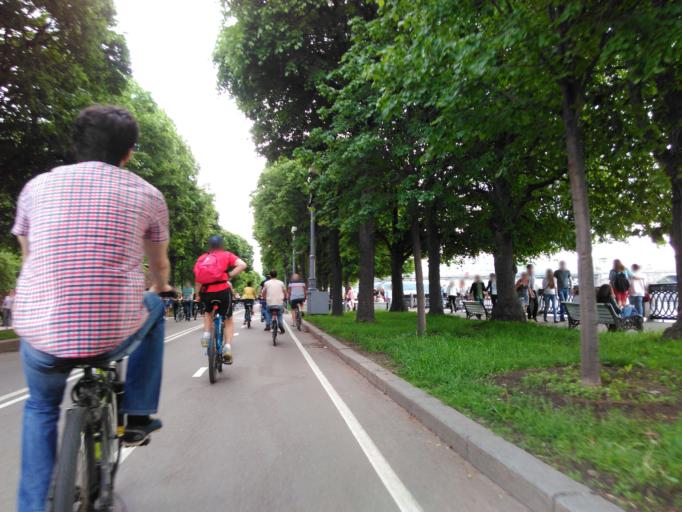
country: RU
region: Moscow
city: Novyye Cheremushki
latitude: 55.7268
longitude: 37.5955
